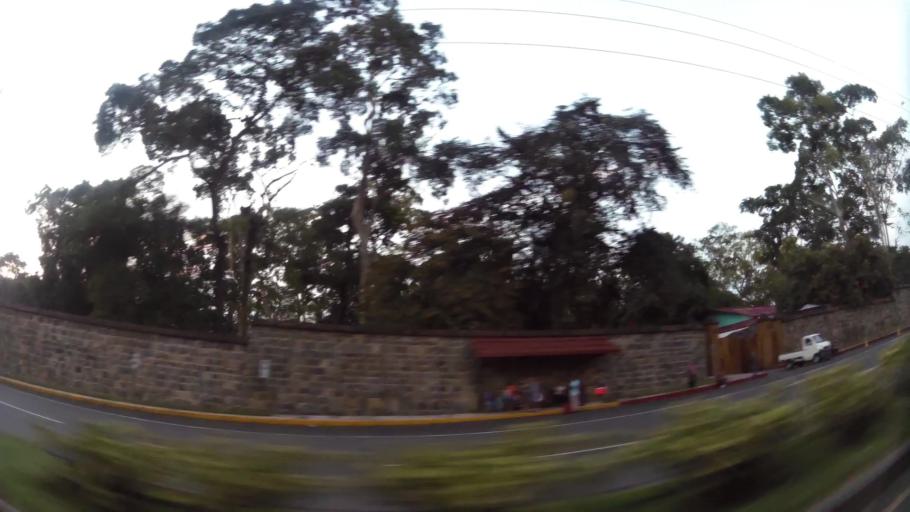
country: GT
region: Retalhuleu
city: Santa Cruz Mulua
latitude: 14.5955
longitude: -91.6163
